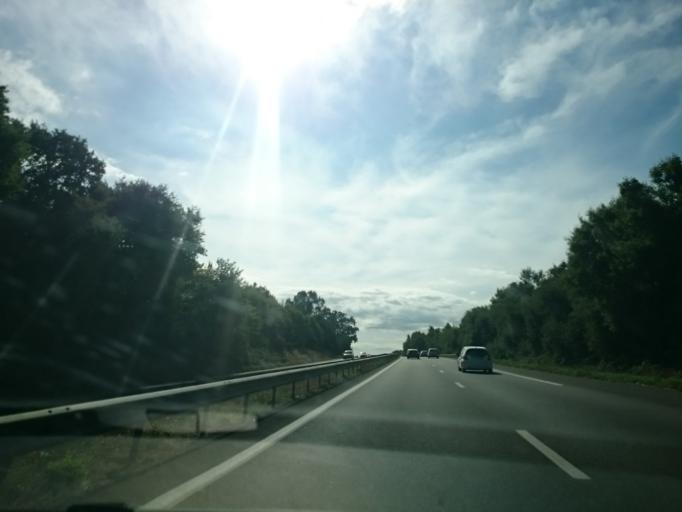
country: FR
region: Brittany
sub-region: Departement d'Ille-et-Vilaine
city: Pace
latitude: 48.1467
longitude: -1.7875
